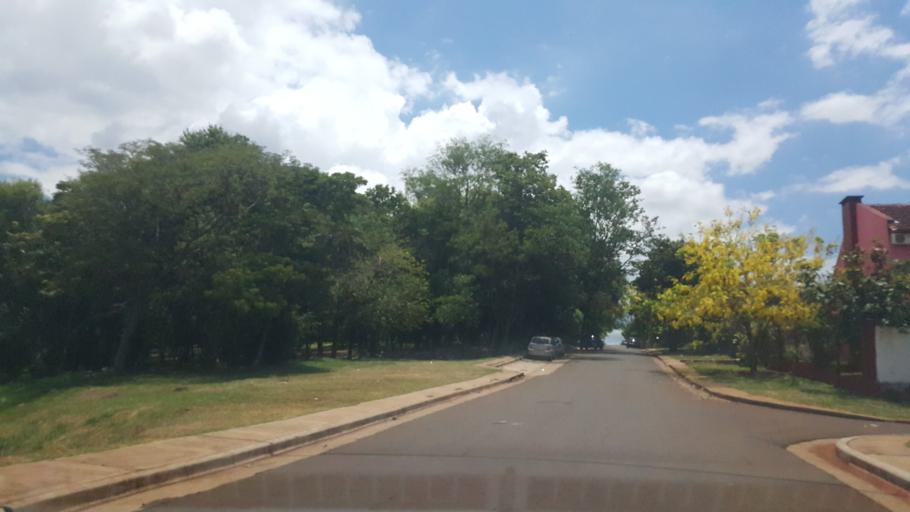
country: AR
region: Misiones
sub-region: Departamento de Capital
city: Posadas
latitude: -27.4065
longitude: -55.8943
